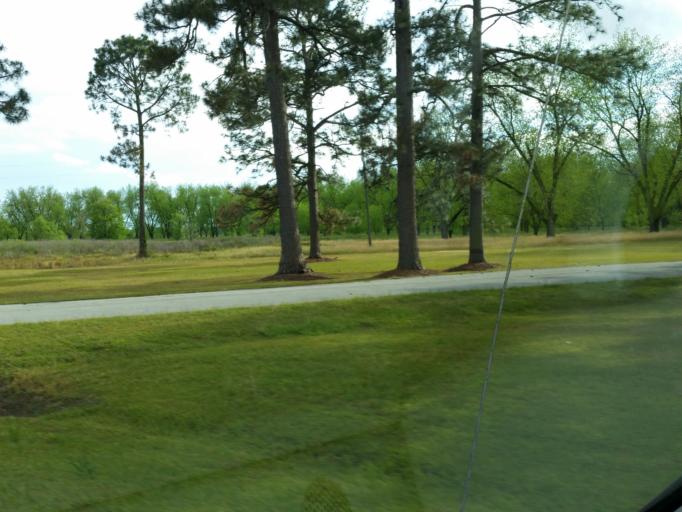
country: US
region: Georgia
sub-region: Dooly County
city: Vienna
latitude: 32.1613
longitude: -83.7609
